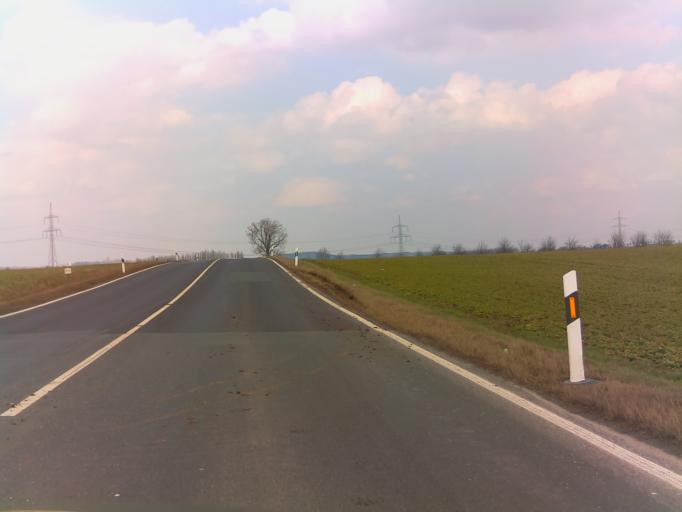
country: DE
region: Thuringia
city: Mattstedt
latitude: 51.0687
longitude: 11.5283
